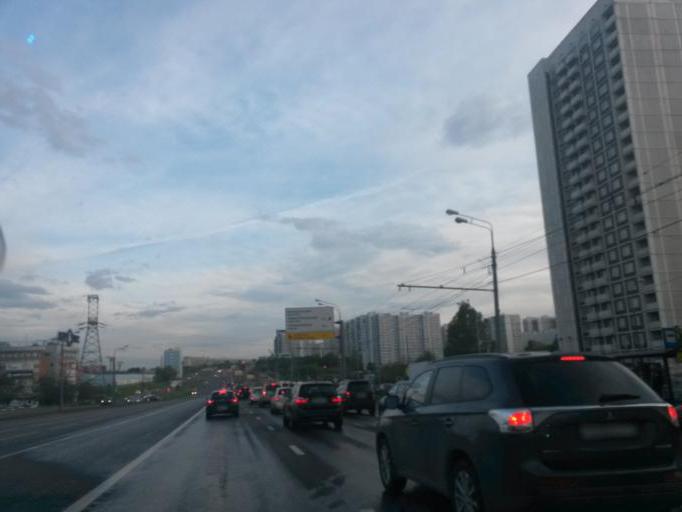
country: RU
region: Moscow
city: Nagornyy
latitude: 55.6425
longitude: 37.6196
